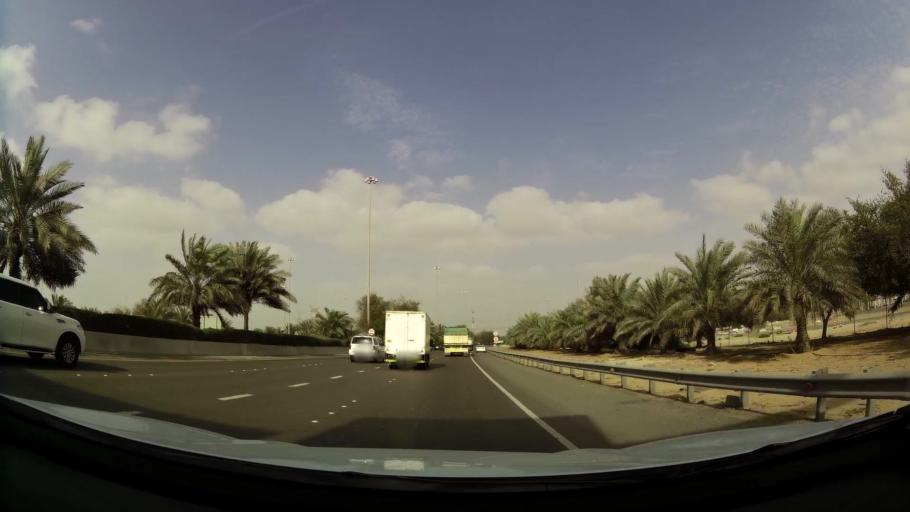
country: AE
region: Abu Dhabi
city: Abu Dhabi
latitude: 24.4184
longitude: 54.5087
